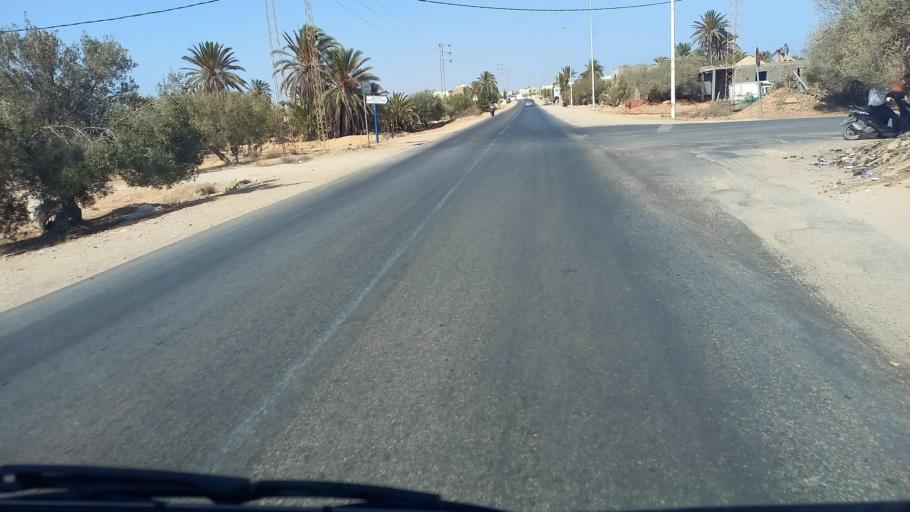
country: TN
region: Madanin
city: Midoun
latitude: 33.7770
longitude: 11.0348
